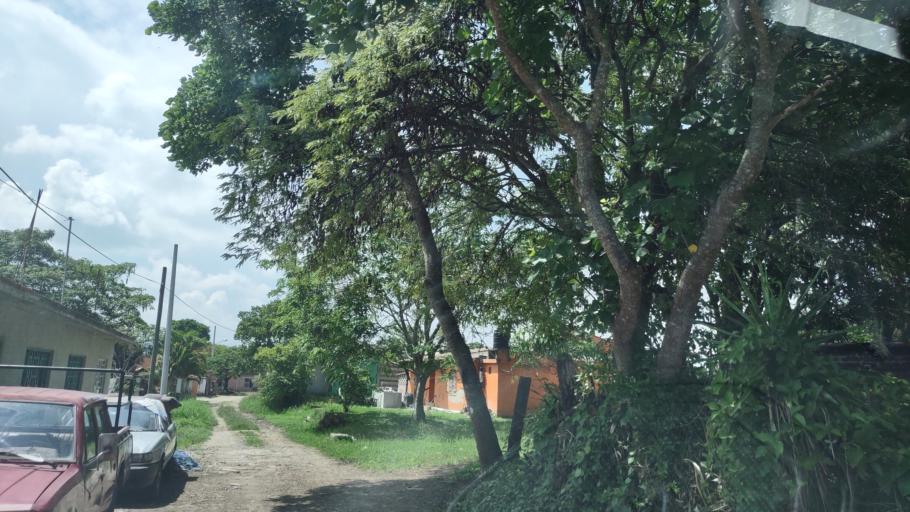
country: MX
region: Veracruz
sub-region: Coatepec
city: Bella Esperanza
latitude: 19.4283
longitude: -96.8106
